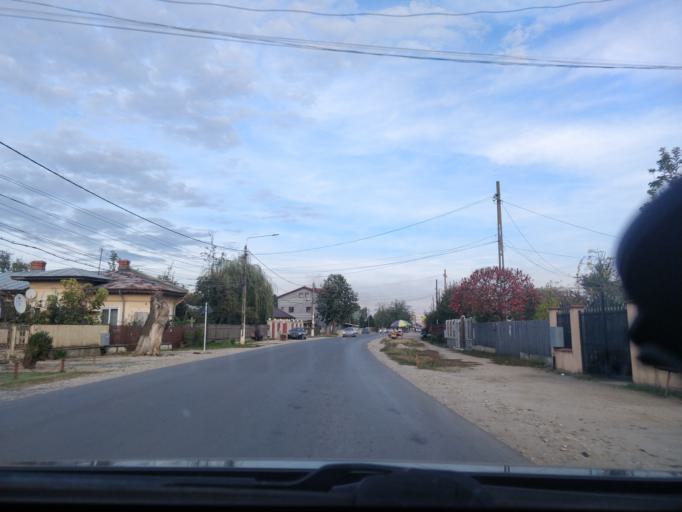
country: RO
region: Giurgiu
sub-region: Comuna Bolintin Vale
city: Bolintin Vale
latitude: 44.4467
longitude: 25.7501
